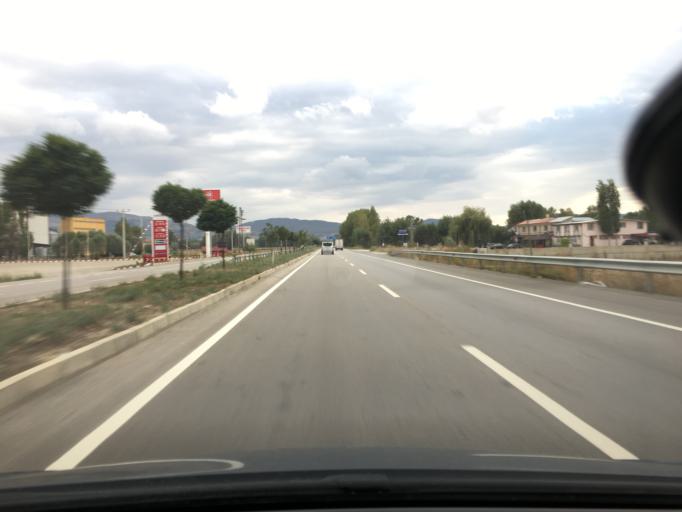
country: TR
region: Afyonkarahisar
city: Sincanli
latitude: 38.7583
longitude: 30.3621
